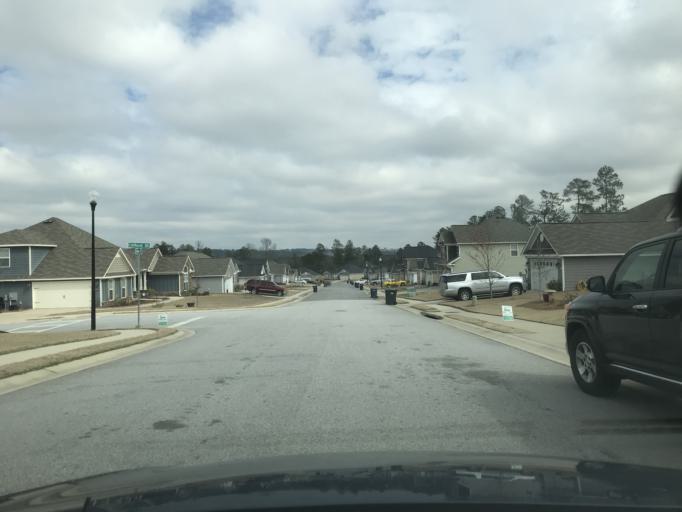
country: US
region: Georgia
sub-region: Columbia County
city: Grovetown
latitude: 33.4436
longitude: -82.1459
